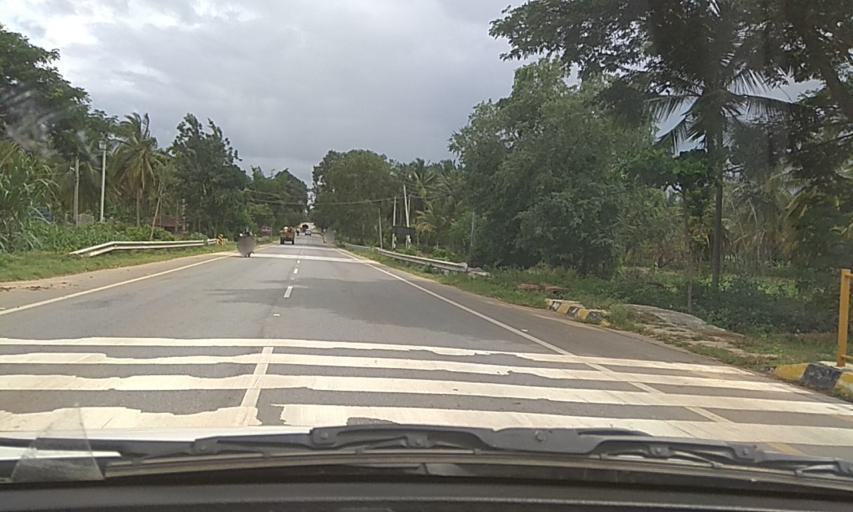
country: IN
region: Karnataka
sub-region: Tumkur
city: Kunigal
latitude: 13.0664
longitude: 77.0256
